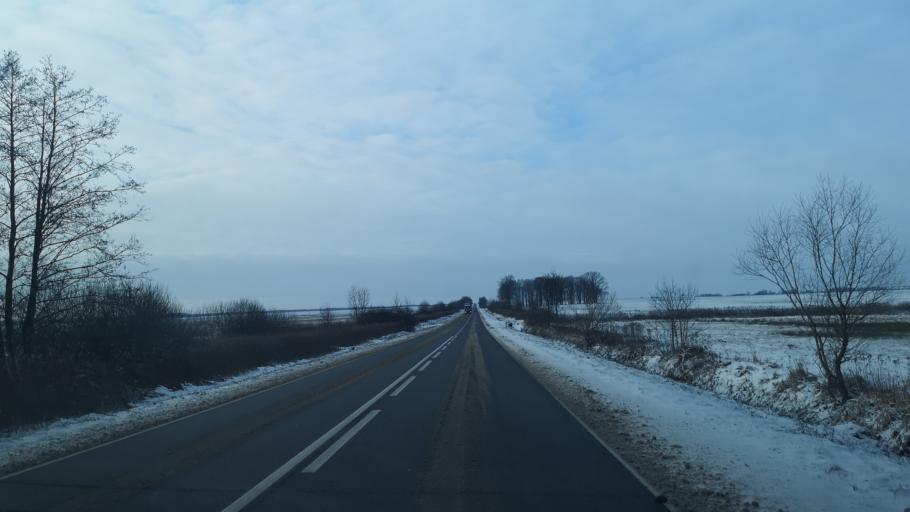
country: PL
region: Subcarpathian Voivodeship
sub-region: Powiat przeworski
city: Adamowka
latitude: 50.2483
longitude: 22.6826
